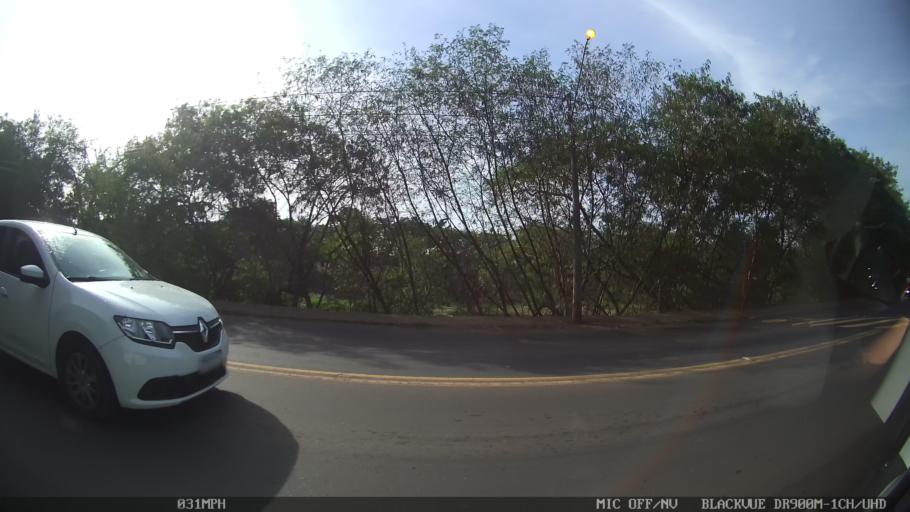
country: BR
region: Sao Paulo
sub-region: Piracicaba
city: Piracicaba
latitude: -22.7151
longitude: -47.6778
